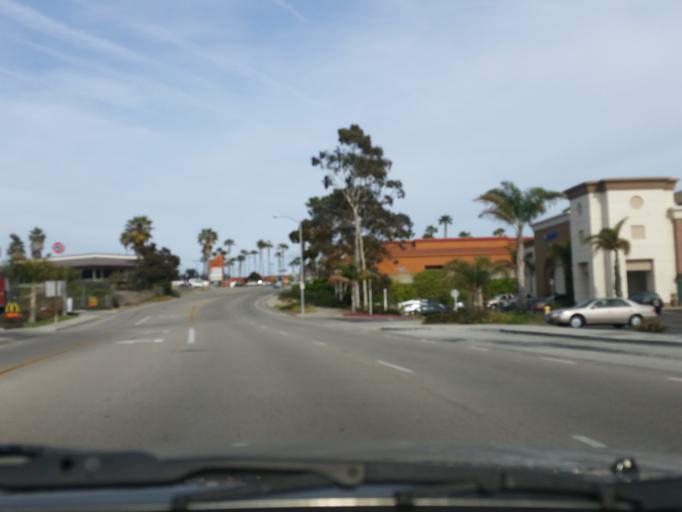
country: US
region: California
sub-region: San Luis Obispo County
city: Grover Beach
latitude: 35.1364
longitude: -120.6267
